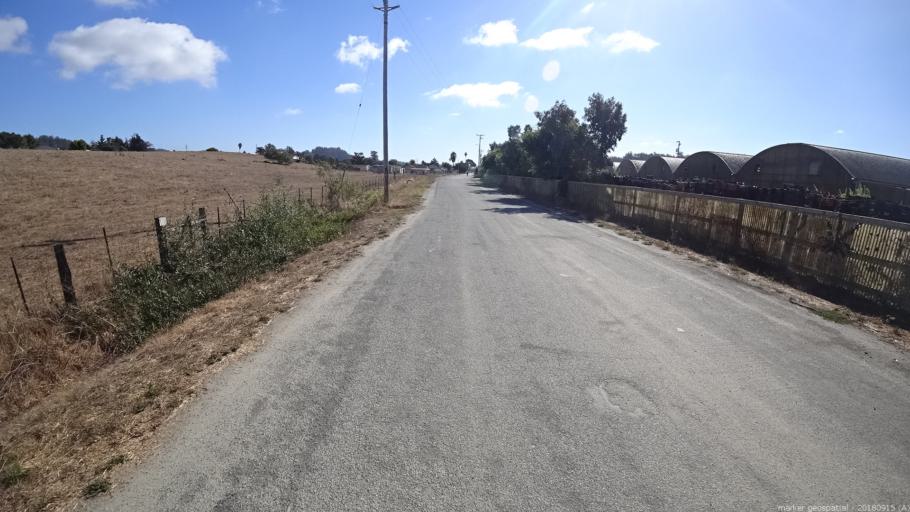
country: US
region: California
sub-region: Monterey County
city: Las Lomas
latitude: 36.8633
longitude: -121.7394
